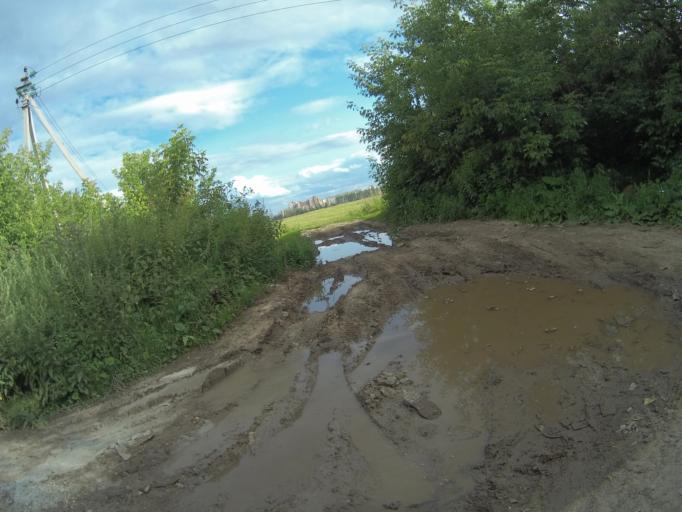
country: RU
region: Vladimir
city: Kommunar
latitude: 56.1815
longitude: 40.4498
